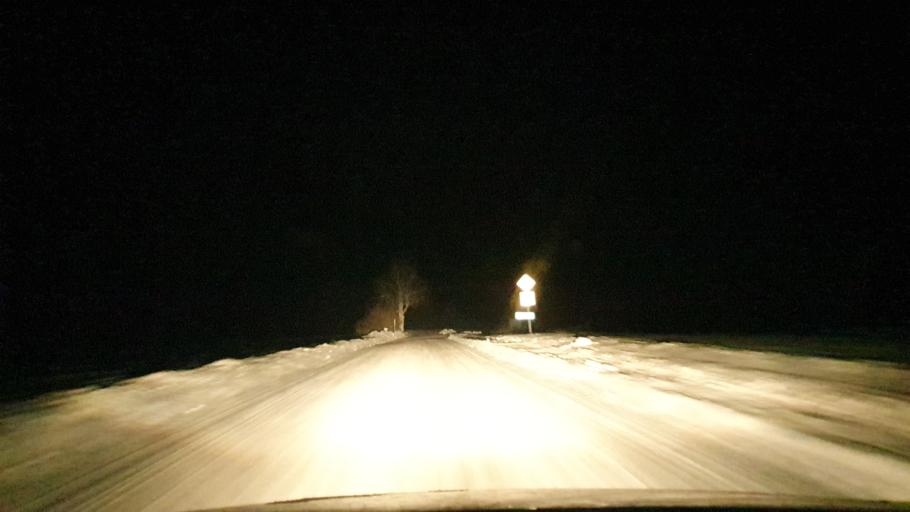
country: EE
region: Vorumaa
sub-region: Antsla vald
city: Vana-Antsla
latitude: 57.9705
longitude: 26.5738
